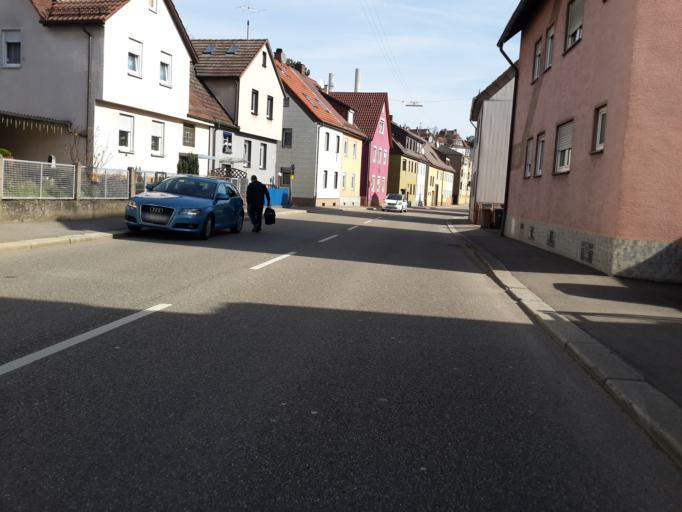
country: DE
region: Baden-Wuerttemberg
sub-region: Regierungsbezirk Stuttgart
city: Neckarsulm
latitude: 49.1680
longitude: 9.1937
